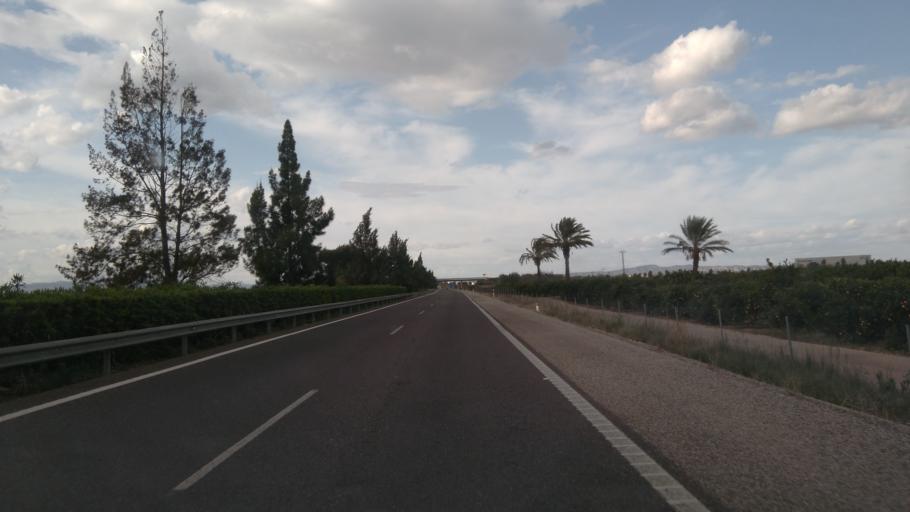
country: ES
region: Valencia
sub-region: Provincia de Valencia
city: Guadassuar
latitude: 39.1669
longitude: -0.4604
